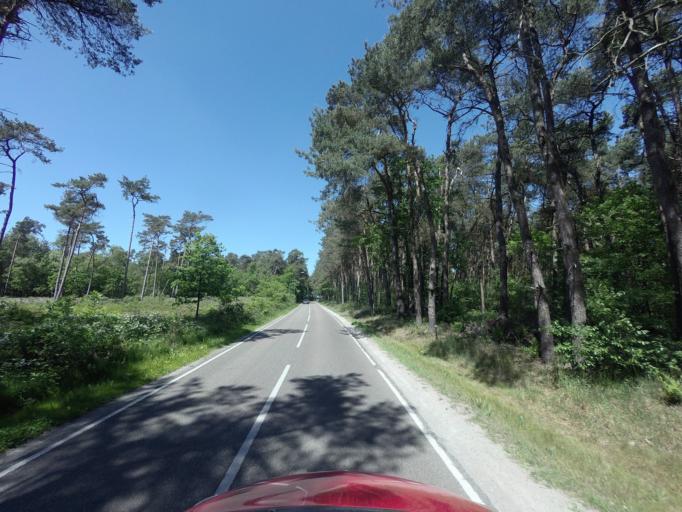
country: NL
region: North Brabant
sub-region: Gemeente Eersel
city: Eersel
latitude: 51.3010
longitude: 5.3004
